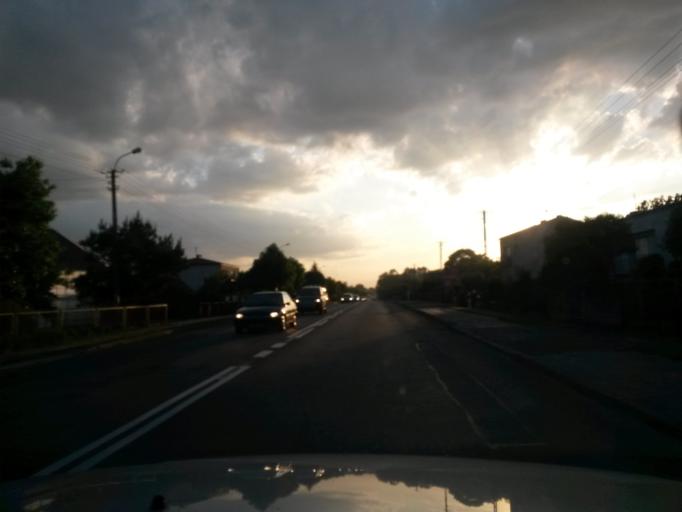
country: PL
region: Lodz Voivodeship
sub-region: Powiat wielunski
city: Mokrsko
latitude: 51.2621
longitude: 18.4707
